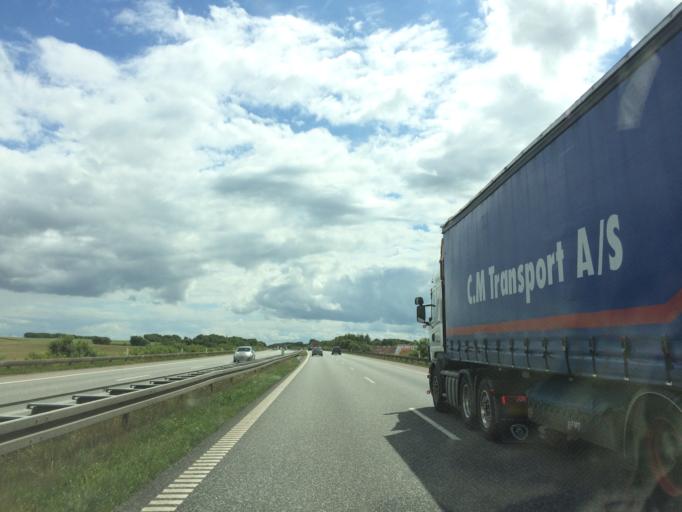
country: DK
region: North Denmark
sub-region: Mariagerfjord Kommune
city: Hobro
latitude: 56.7416
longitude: 9.6994
